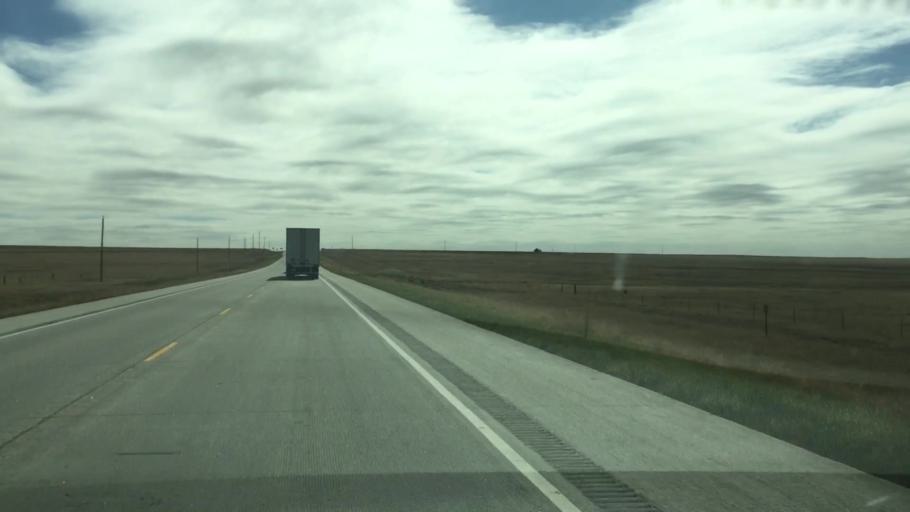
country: US
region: Colorado
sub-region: Lincoln County
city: Hugo
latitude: 38.9953
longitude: -103.2795
